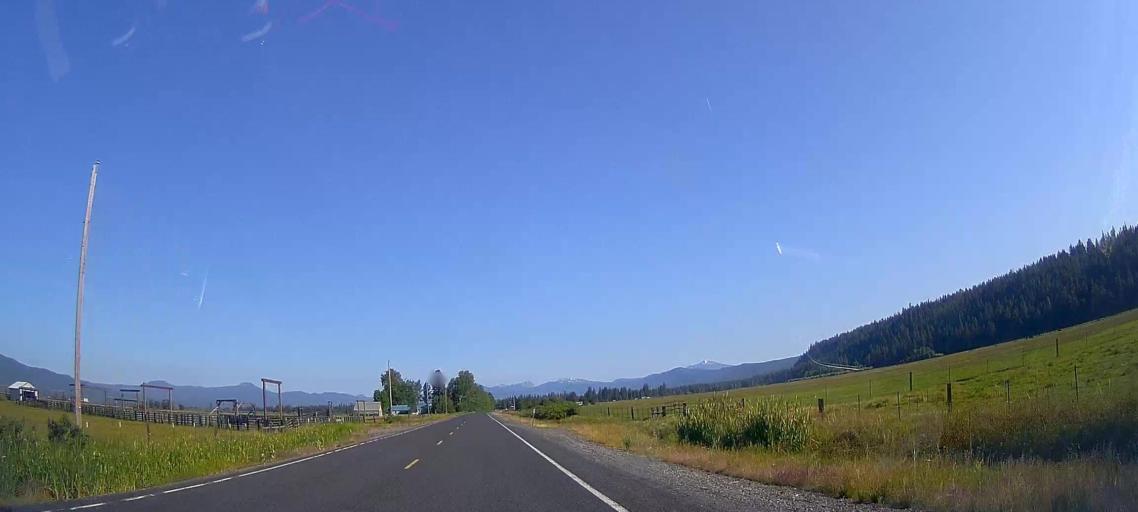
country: US
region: Oregon
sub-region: Klamath County
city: Klamath Falls
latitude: 42.6606
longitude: -121.9632
